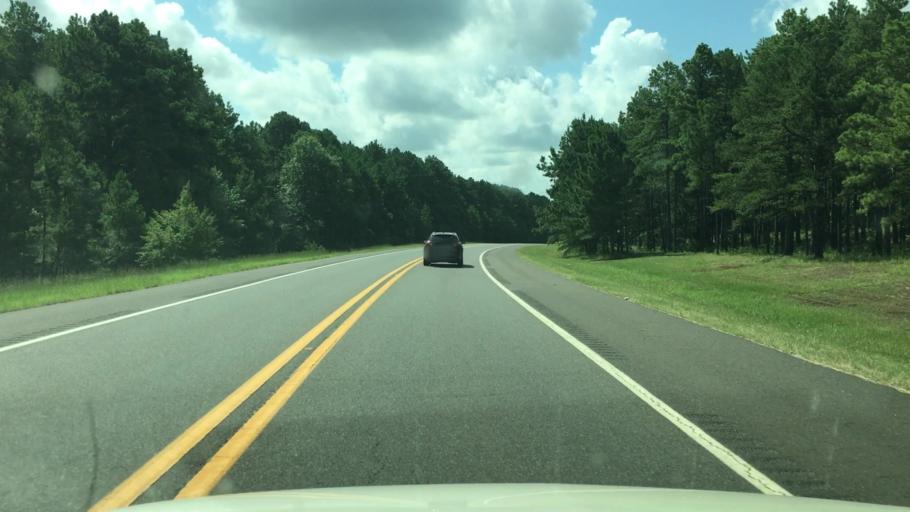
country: US
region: Arkansas
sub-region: Clark County
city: Arkadelphia
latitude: 34.2256
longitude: -93.0884
